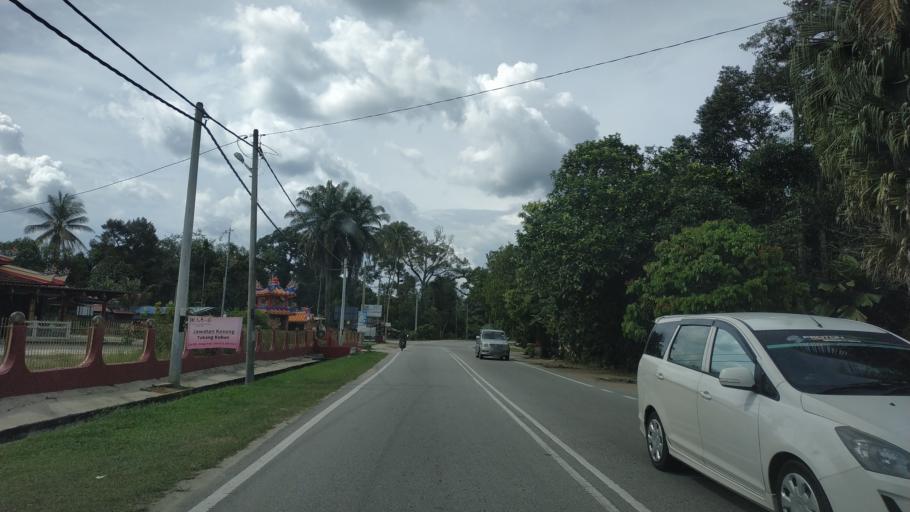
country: MY
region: Kedah
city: Kulim
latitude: 5.4216
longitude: 100.6662
